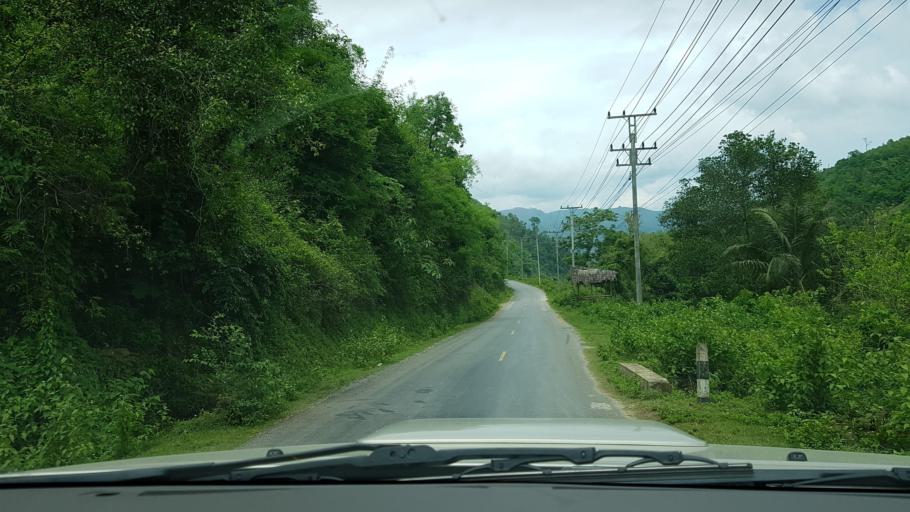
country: TH
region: Nan
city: Chaloem Phra Kiat
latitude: 19.9340
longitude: 101.1774
